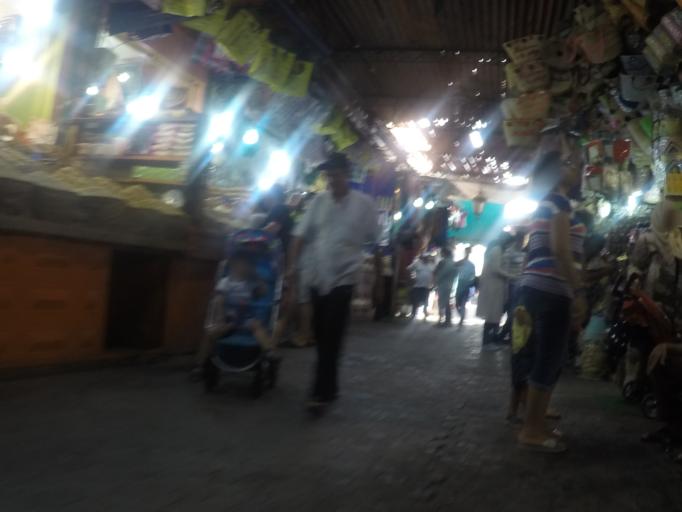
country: MA
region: Marrakech-Tensift-Al Haouz
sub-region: Marrakech
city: Marrakesh
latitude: 31.6274
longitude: -7.9881
